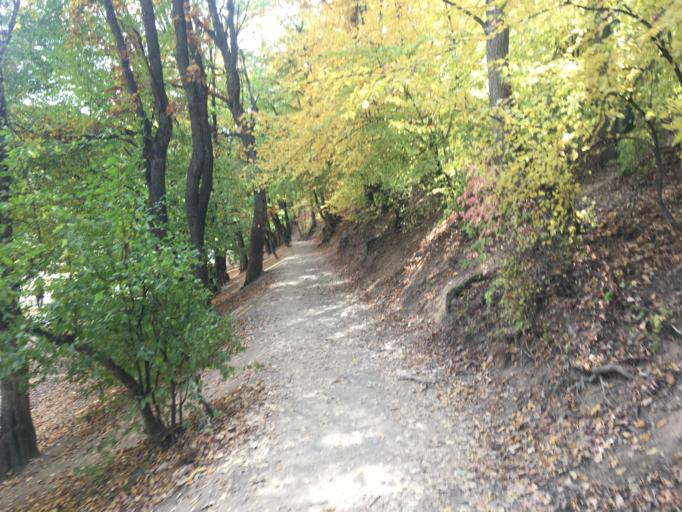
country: XK
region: Pristina
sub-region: Komuna e Prishtines
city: Pristina
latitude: 42.6725
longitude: 21.2152
